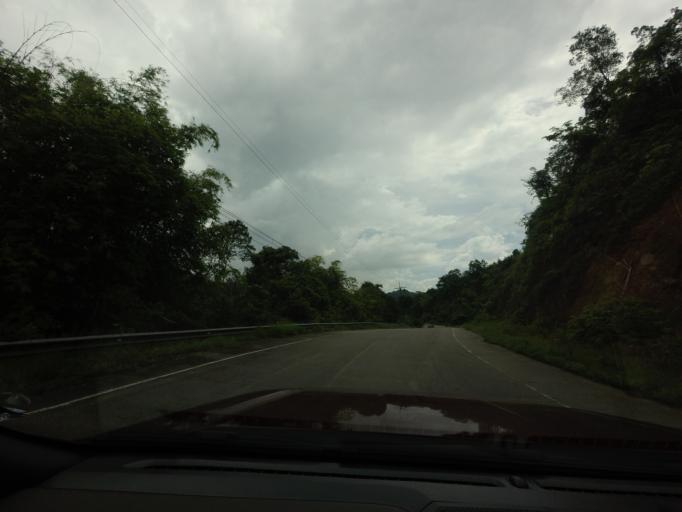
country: TH
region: Narathiwat
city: Sukhirin
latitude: 5.9808
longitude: 101.6933
